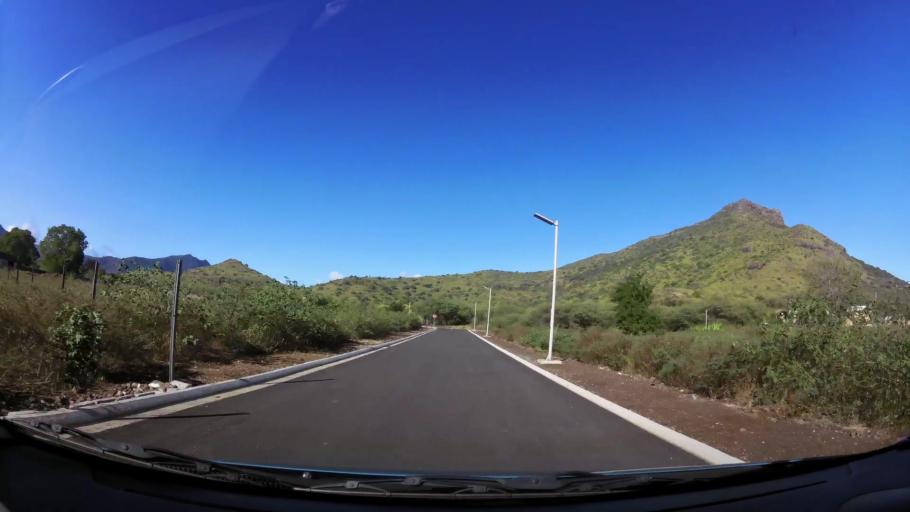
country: MU
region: Black River
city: Tamarin
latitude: -20.3391
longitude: 57.3901
